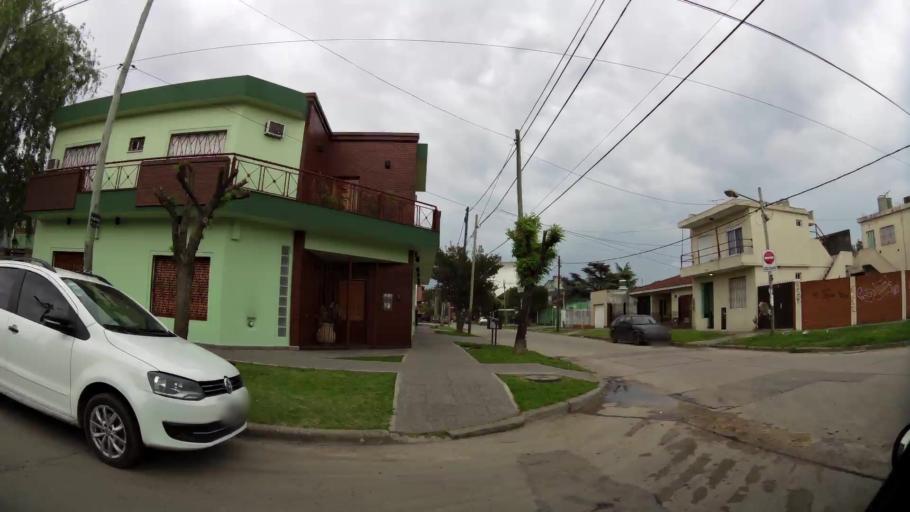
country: AR
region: Buenos Aires
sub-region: Partido de Quilmes
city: Quilmes
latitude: -34.7996
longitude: -58.2768
